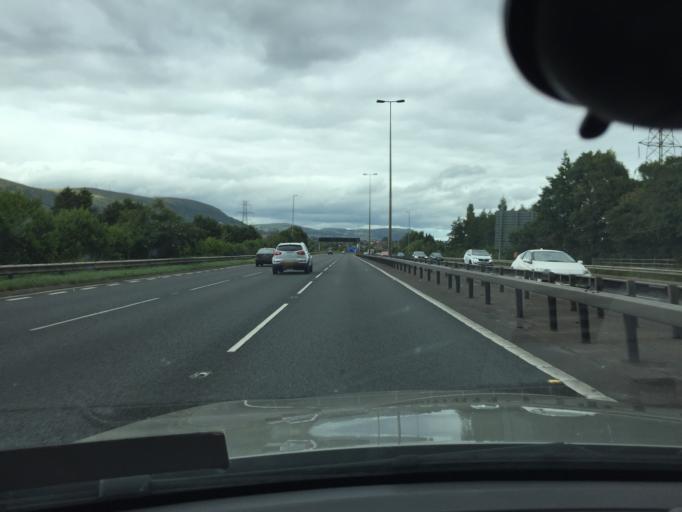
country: GB
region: Northern Ireland
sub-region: Lisburn District
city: Lisburn
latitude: 54.5624
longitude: -5.9938
